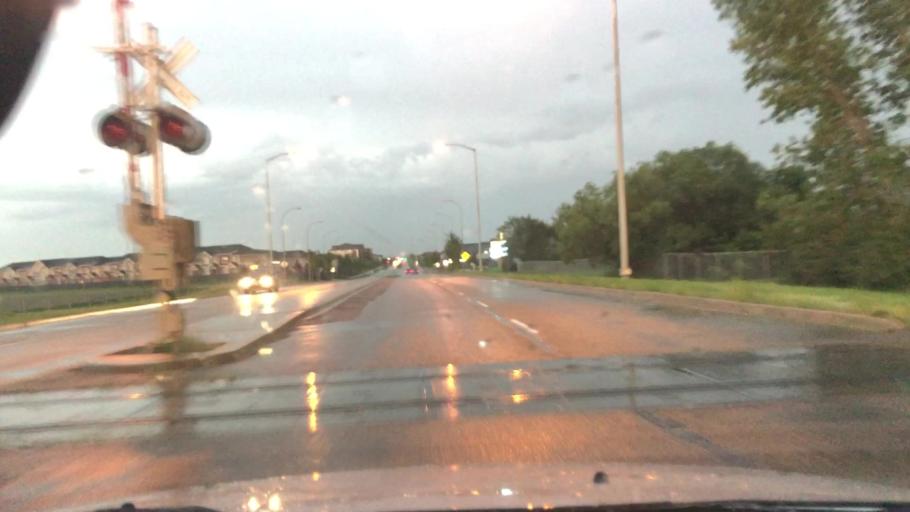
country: CA
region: Alberta
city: St. Albert
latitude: 53.6287
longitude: -113.5656
